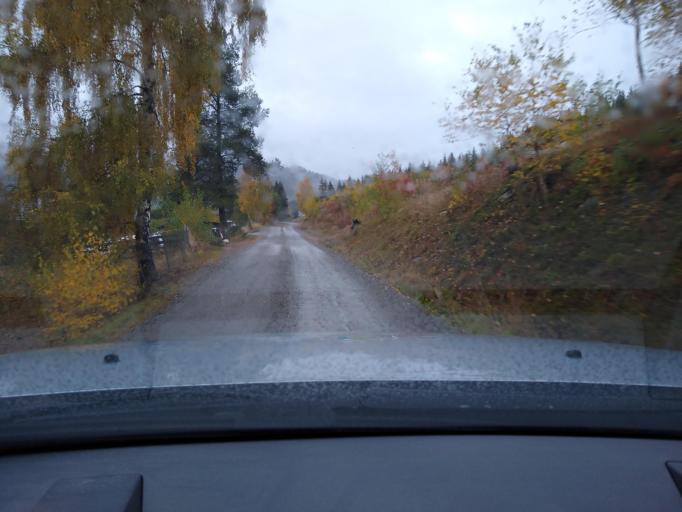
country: NO
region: Oppland
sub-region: Ringebu
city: Ringebu
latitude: 61.5420
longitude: 10.1495
